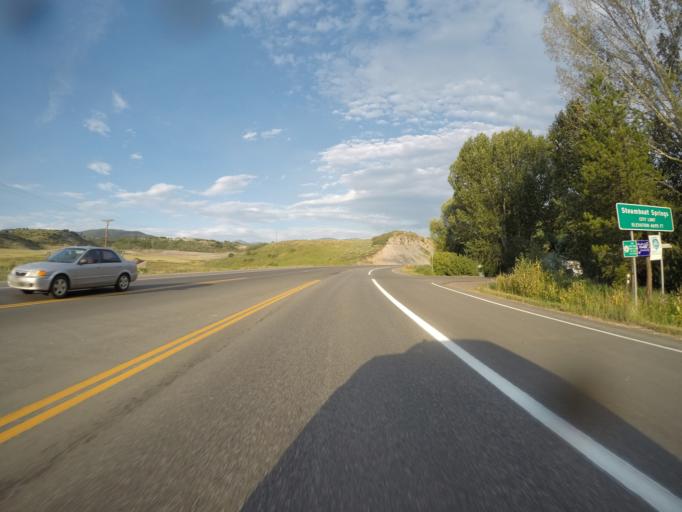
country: US
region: Colorado
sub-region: Routt County
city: Steamboat Springs
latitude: 40.5063
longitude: -106.8800
